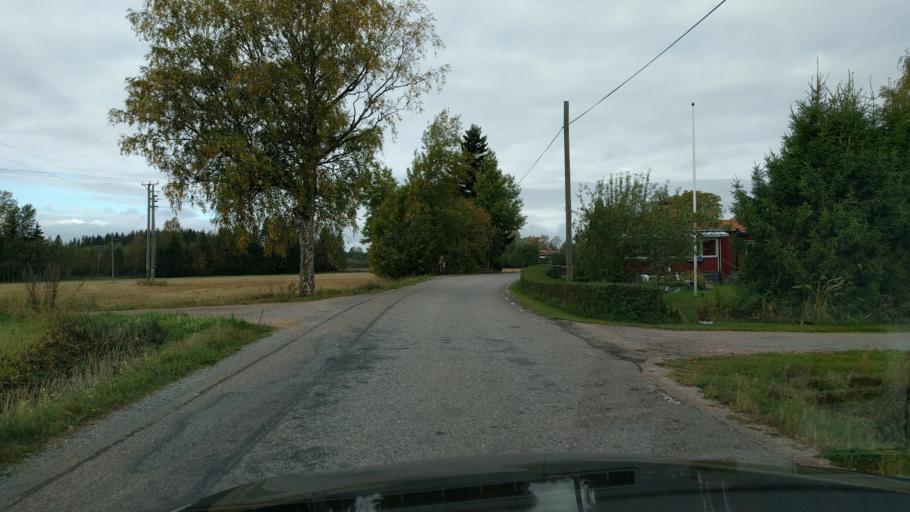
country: SE
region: Uppsala
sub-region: Osthammars Kommun
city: Bjorklinge
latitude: 60.1574
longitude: 17.5441
